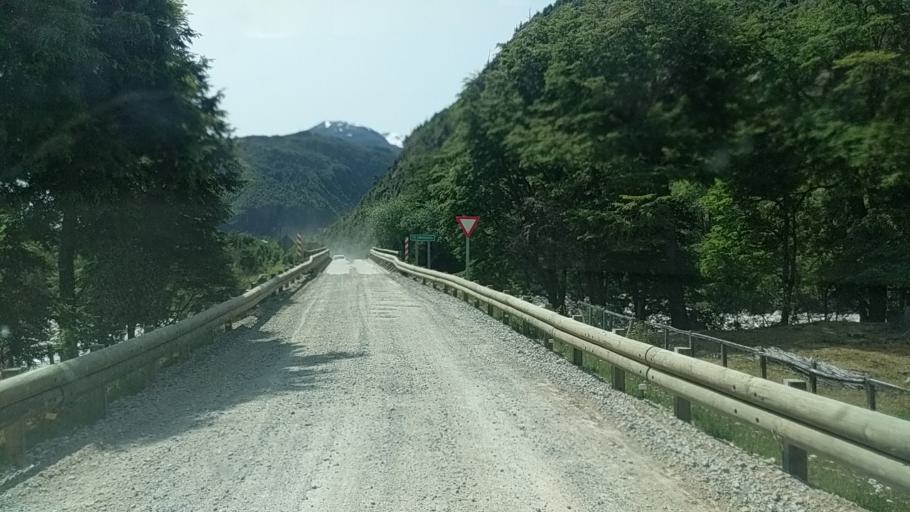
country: CL
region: Los Lagos
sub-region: Provincia de Palena
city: Palena
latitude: -43.4665
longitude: -72.1186
